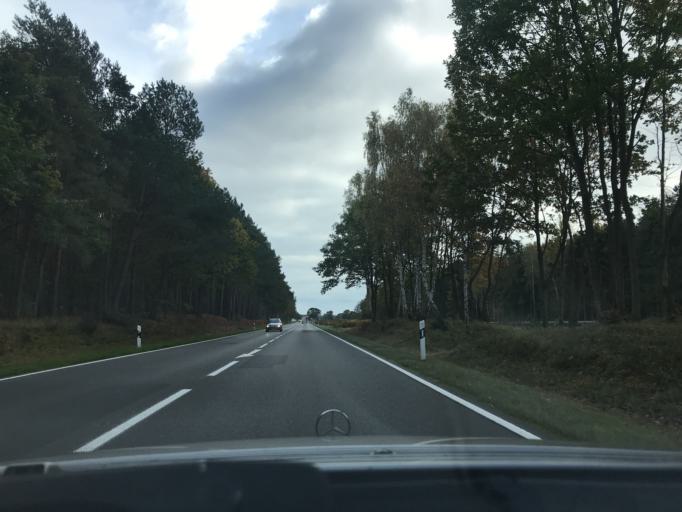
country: DE
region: Mecklenburg-Vorpommern
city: Koserow
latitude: 54.0572
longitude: 13.9865
